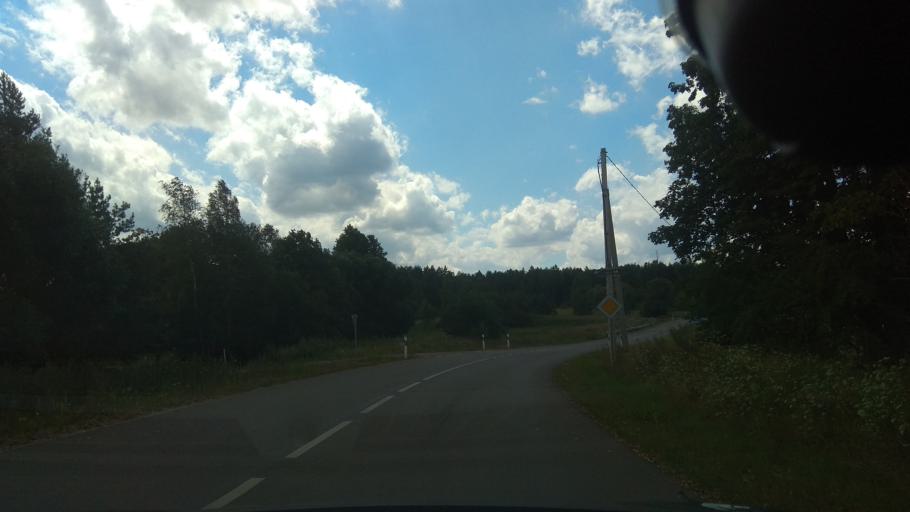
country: LT
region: Vilnius County
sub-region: Trakai
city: Rudiskes
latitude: 54.5099
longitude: 24.8767
